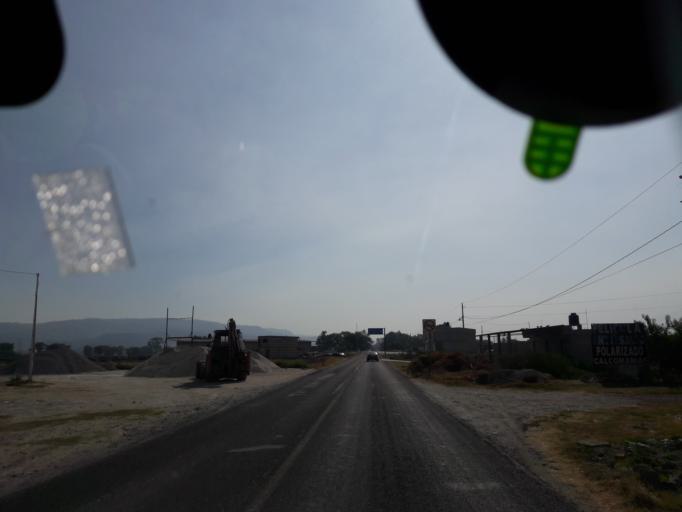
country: MX
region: Tlaxcala
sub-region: Ixtacuixtla de Mariano Matamoros
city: Santa Justina Ecatepec
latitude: 19.3135
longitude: -98.3357
